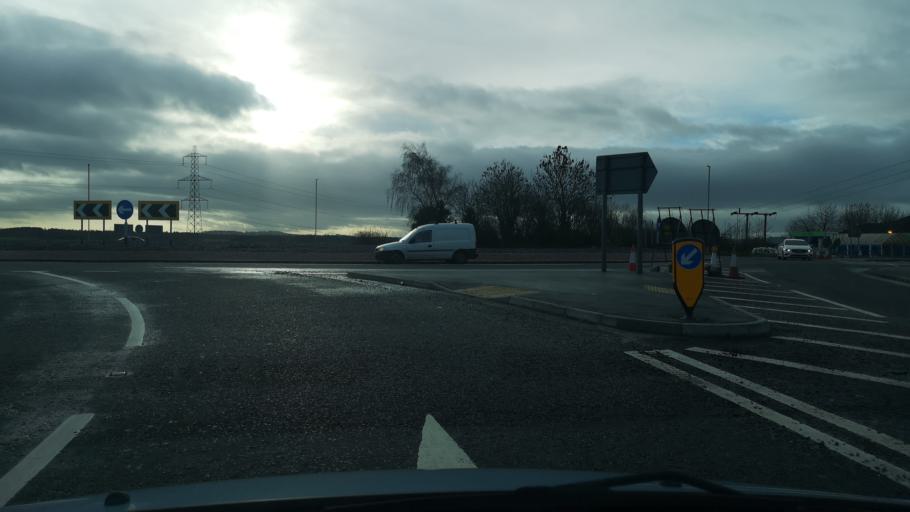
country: GB
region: England
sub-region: Barnsley
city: Little Houghton
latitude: 53.5342
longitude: -1.3541
